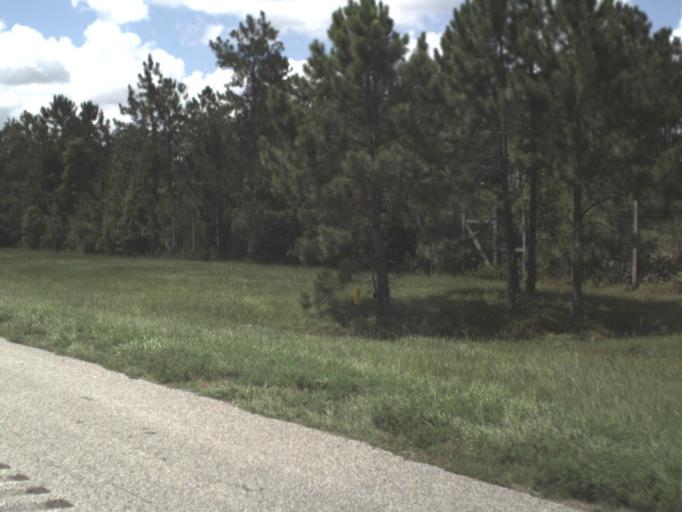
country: US
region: Florida
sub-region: Saint Johns County
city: Saint Augustine Shores
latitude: 29.7565
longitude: -81.3502
